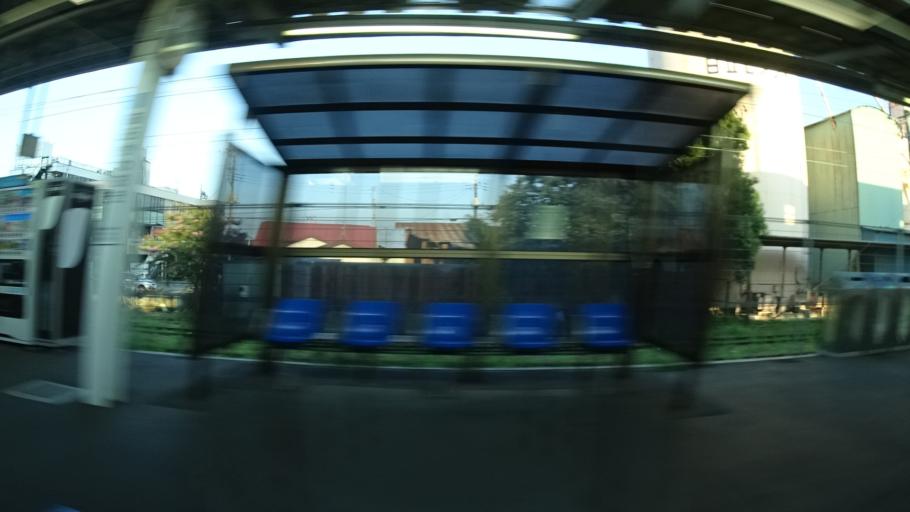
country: JP
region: Ibaraki
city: Naka
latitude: 36.0314
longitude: 140.1667
